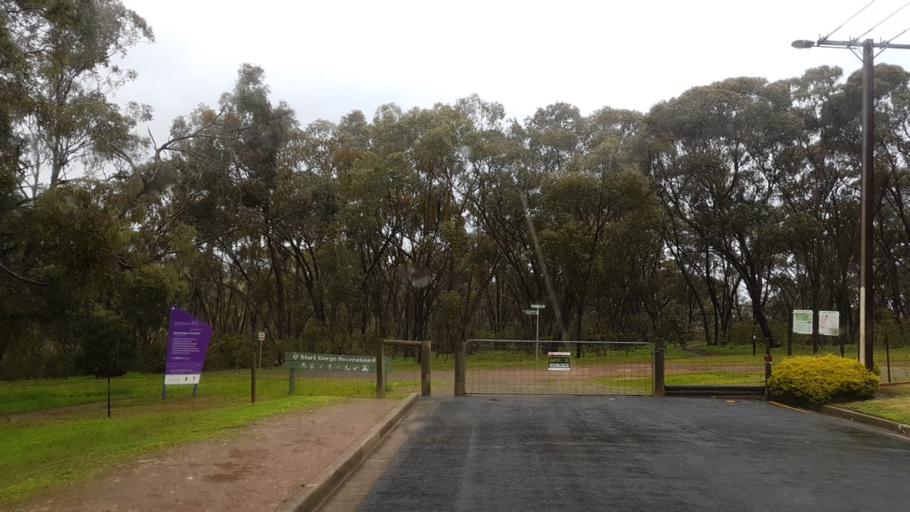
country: AU
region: South Australia
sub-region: Onkaparinga
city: Bedford Park
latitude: -35.0425
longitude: 138.5875
